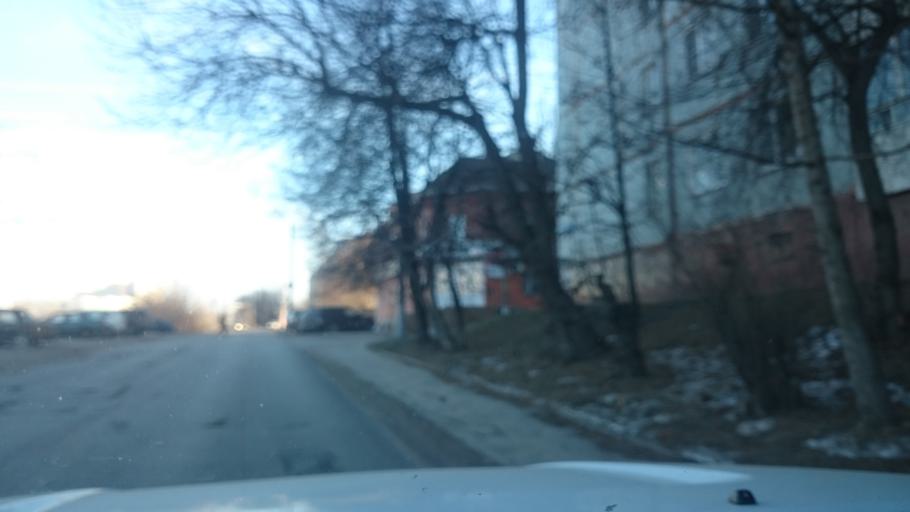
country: RU
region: Tula
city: Tula
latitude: 54.2057
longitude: 37.6807
